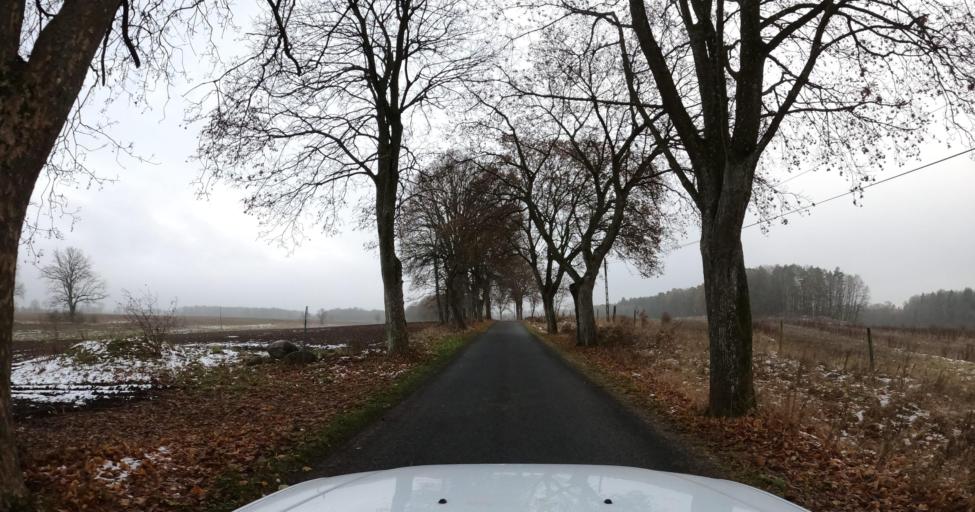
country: PL
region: West Pomeranian Voivodeship
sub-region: Powiat swidwinski
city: Swidwin
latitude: 53.8696
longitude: 15.8298
